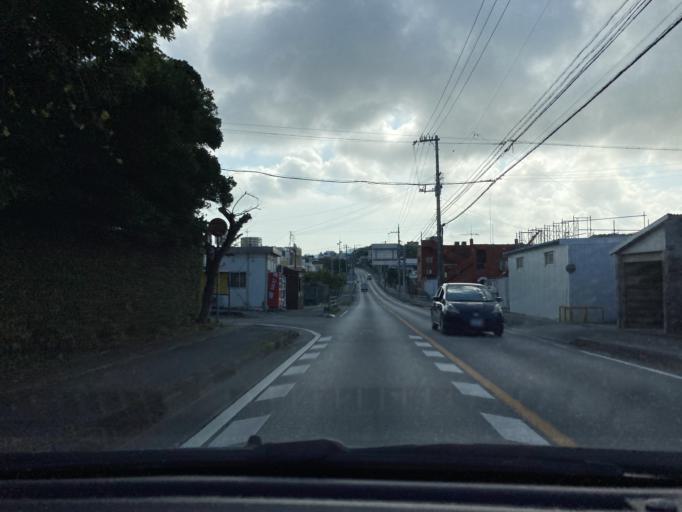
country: JP
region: Okinawa
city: Tomigusuku
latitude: 26.1725
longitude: 127.7294
